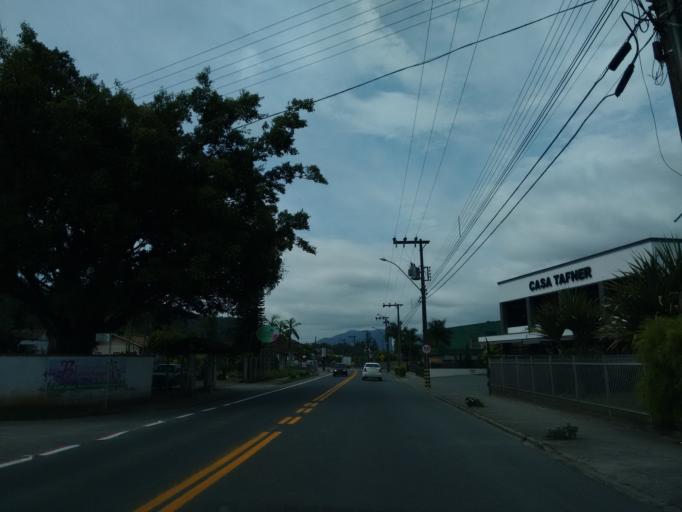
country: BR
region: Santa Catarina
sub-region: Pomerode
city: Pomerode
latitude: -26.7167
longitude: -49.1672
